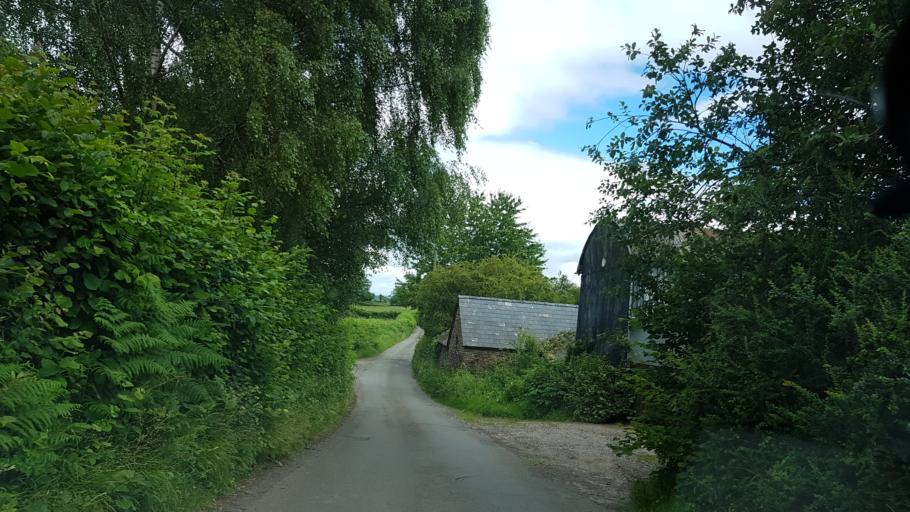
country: GB
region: Wales
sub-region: Monmouthshire
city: Llanarth
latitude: 51.7943
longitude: -2.8258
